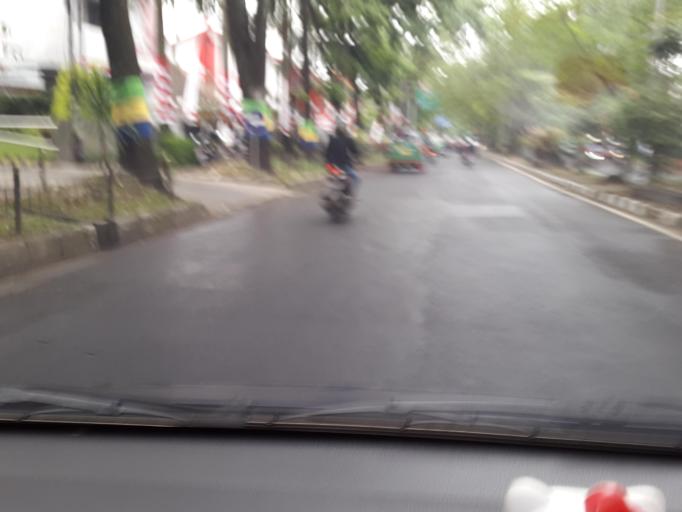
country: ID
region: West Java
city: Bandung
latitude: -6.9051
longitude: 107.6290
